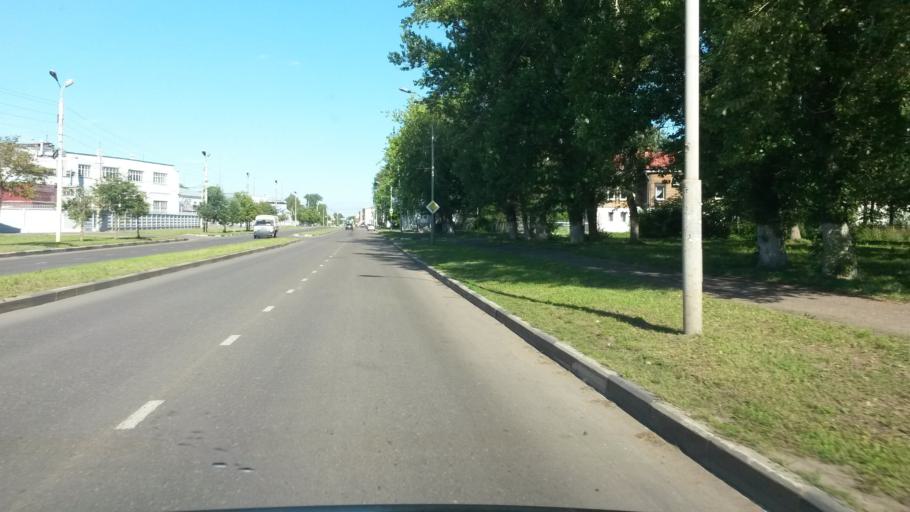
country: RU
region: Jaroslavl
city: Yaroslavl
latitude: 57.6077
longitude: 39.8511
